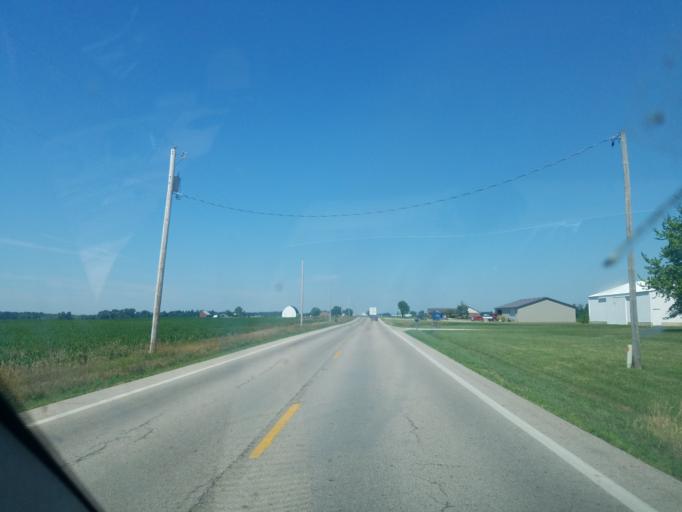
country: US
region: Ohio
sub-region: Shelby County
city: Botkins
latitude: 40.4385
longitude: -84.2130
